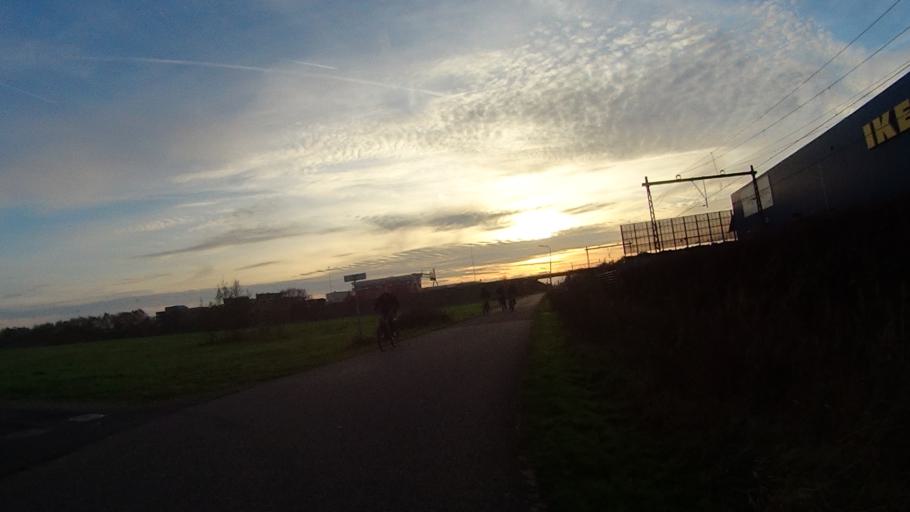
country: NL
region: Utrecht
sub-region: Gemeente Amersfoort
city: Randenbroek
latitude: 52.1844
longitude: 5.4204
